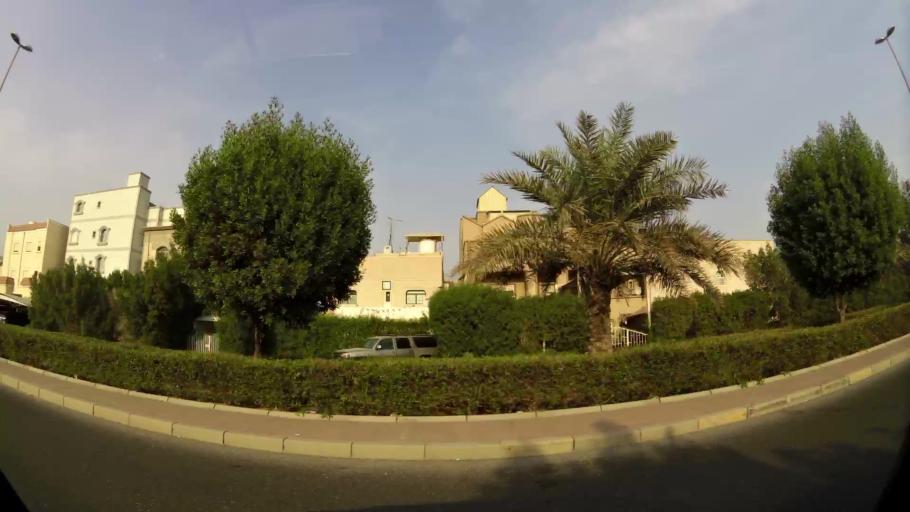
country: KW
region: Mubarak al Kabir
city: Mubarak al Kabir
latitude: 29.2148
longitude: 48.0646
